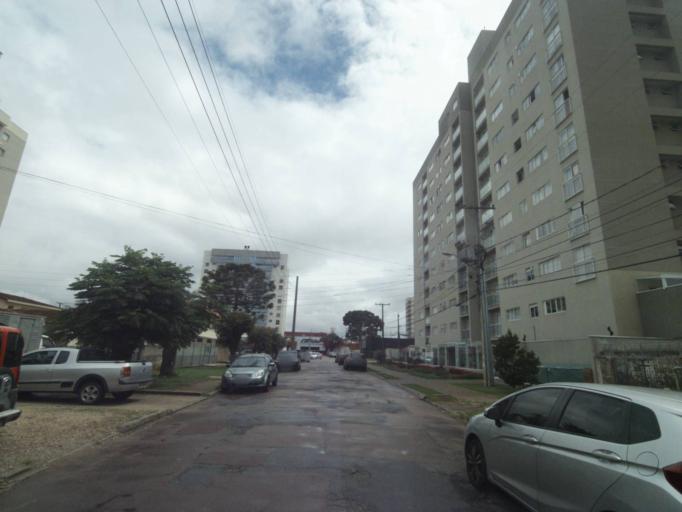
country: BR
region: Parana
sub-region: Curitiba
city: Curitiba
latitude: -25.4879
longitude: -49.2955
